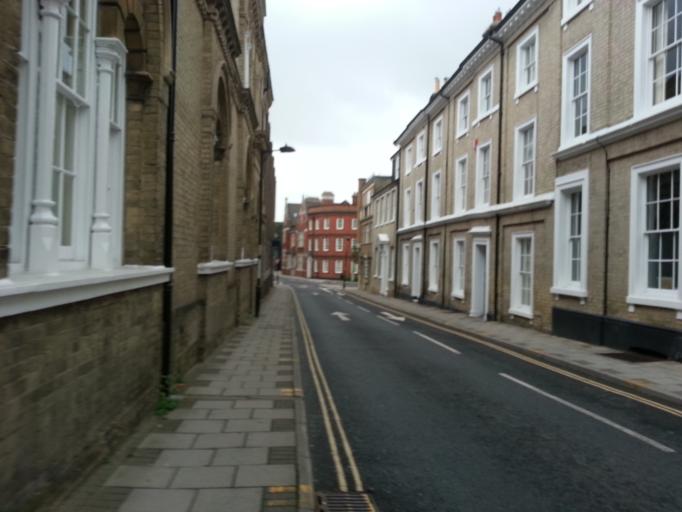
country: GB
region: England
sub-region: Suffolk
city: Ipswich
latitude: 52.0574
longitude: 1.1506
